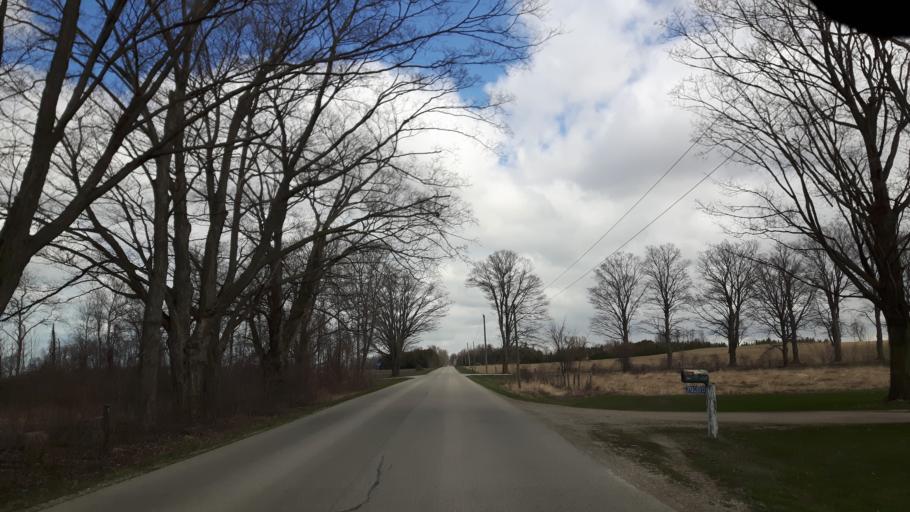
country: CA
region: Ontario
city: Goderich
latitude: 43.6788
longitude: -81.6847
